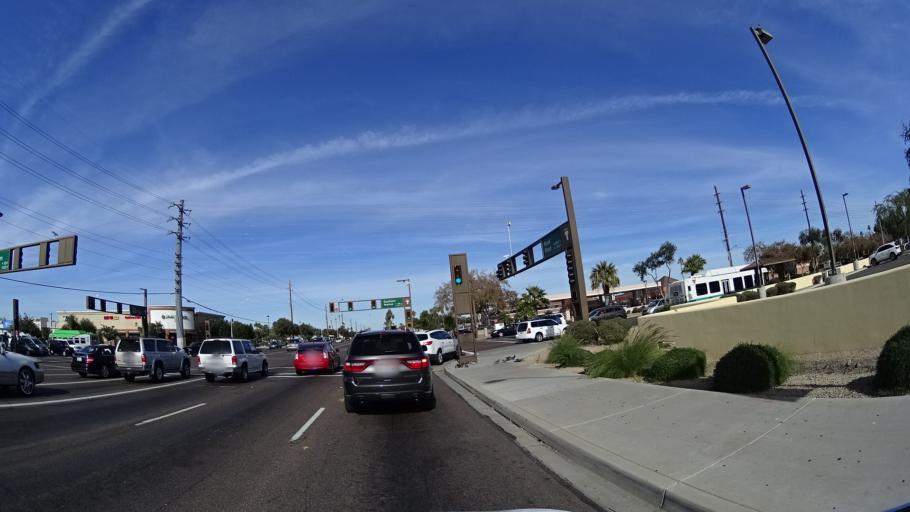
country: US
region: Arizona
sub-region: Maricopa County
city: Tempe Junction
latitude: 33.3926
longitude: -111.9262
